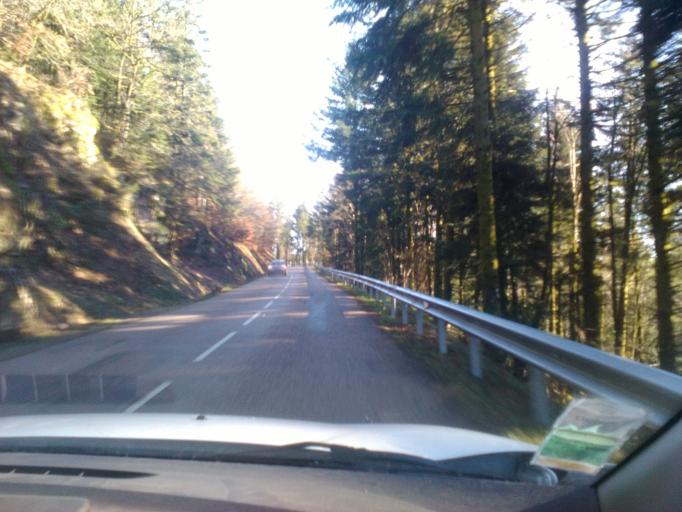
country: FR
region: Lorraine
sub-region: Departement des Vosges
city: Remiremont
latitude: 47.9700
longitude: 6.5327
